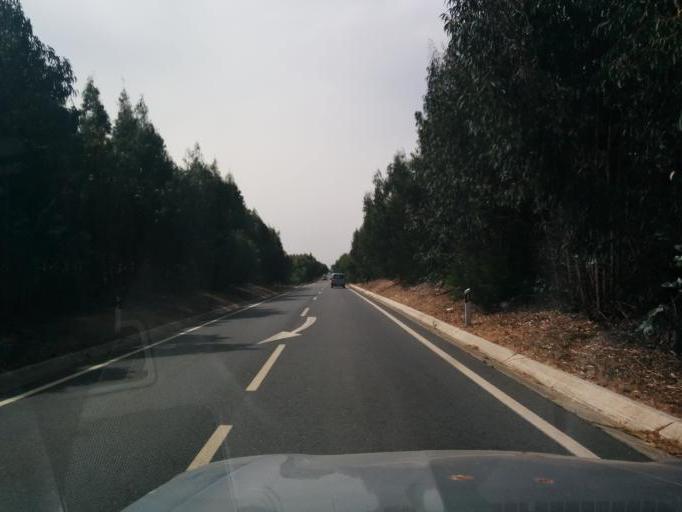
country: PT
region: Beja
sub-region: Odemira
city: Vila Nova de Milfontes
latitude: 37.6682
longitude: -8.7596
